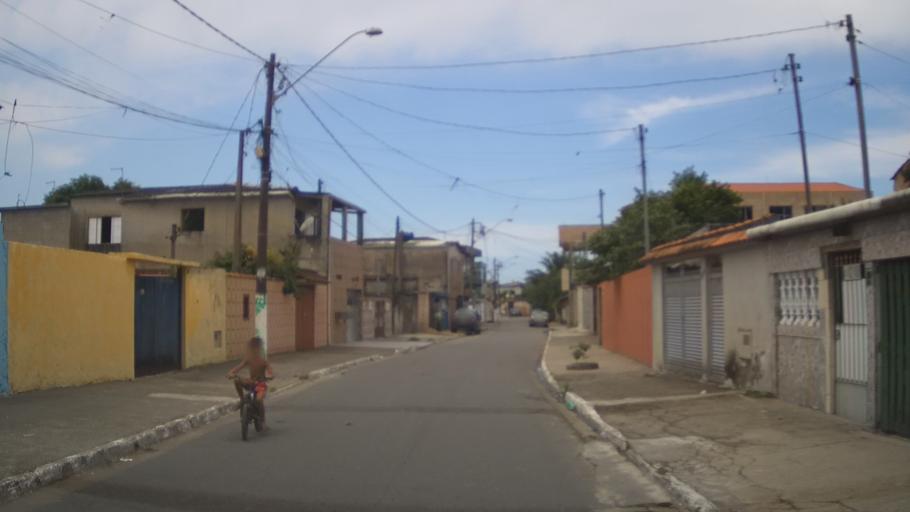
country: BR
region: Sao Paulo
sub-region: Praia Grande
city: Praia Grande
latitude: -24.0215
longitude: -46.4944
